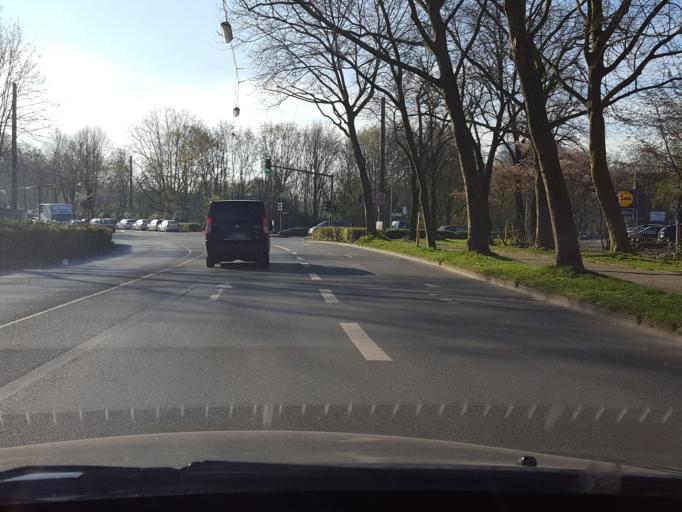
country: DE
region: North Rhine-Westphalia
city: Datteln
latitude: 51.6504
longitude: 7.3311
